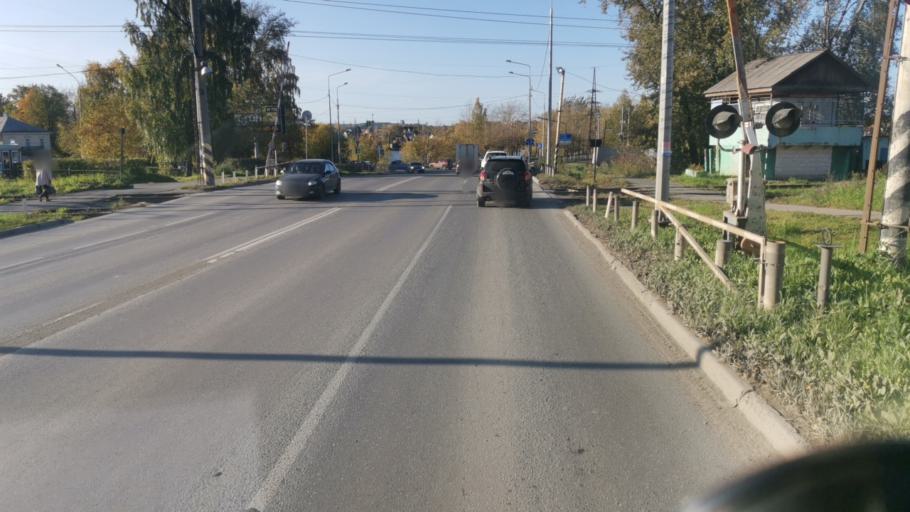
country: RU
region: Sverdlovsk
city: Nizhniy Tagil
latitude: 57.9263
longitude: 59.9379
